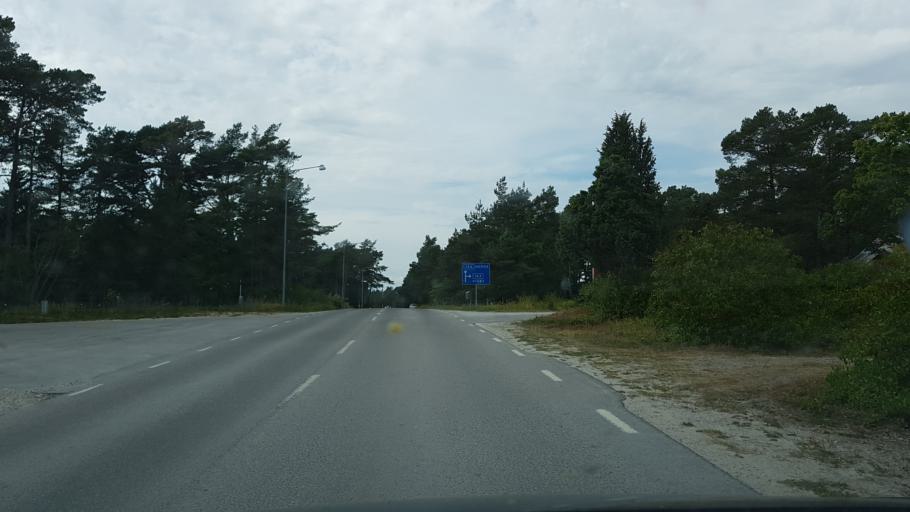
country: SE
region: Gotland
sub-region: Gotland
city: Hemse
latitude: 57.3391
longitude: 18.6973
